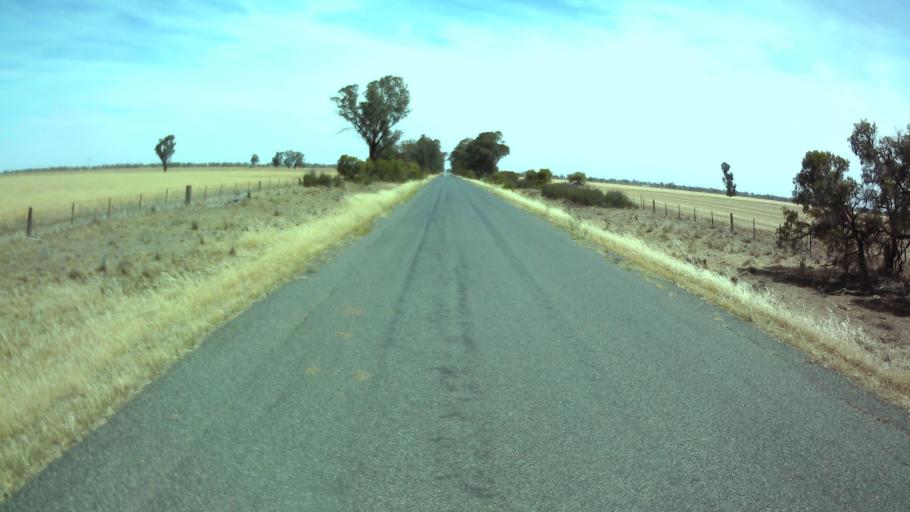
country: AU
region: New South Wales
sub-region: Weddin
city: Grenfell
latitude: -33.9699
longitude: 147.7801
